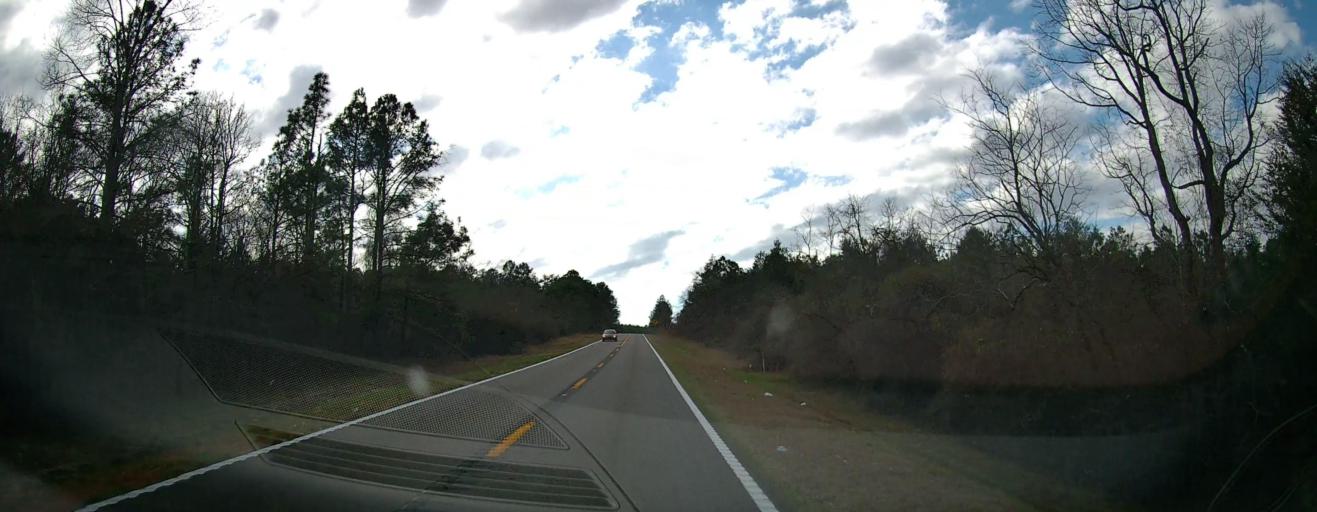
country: US
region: Georgia
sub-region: Marion County
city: Buena Vista
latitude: 32.4387
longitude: -84.5004
